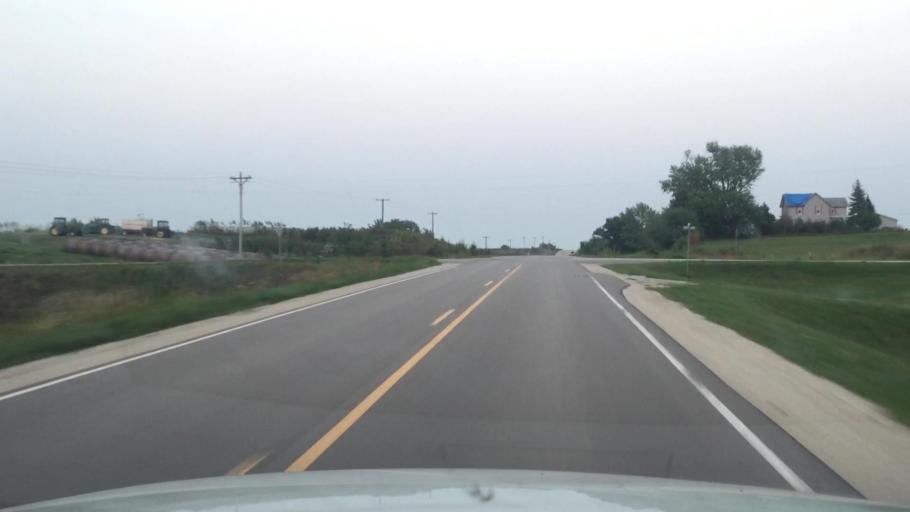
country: US
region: Iowa
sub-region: Warren County
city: Indianola
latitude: 41.1825
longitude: -93.4620
